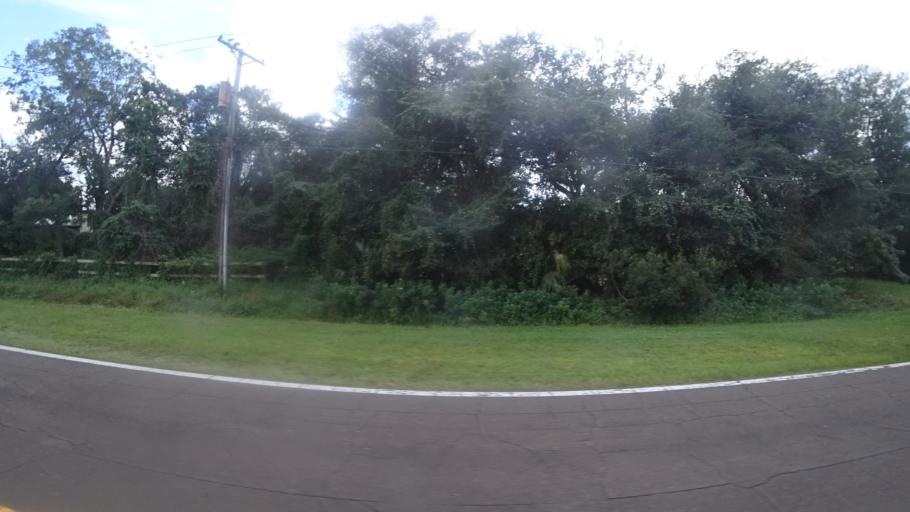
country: US
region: Florida
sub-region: Hillsborough County
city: Ruskin
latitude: 27.6478
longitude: -82.4169
